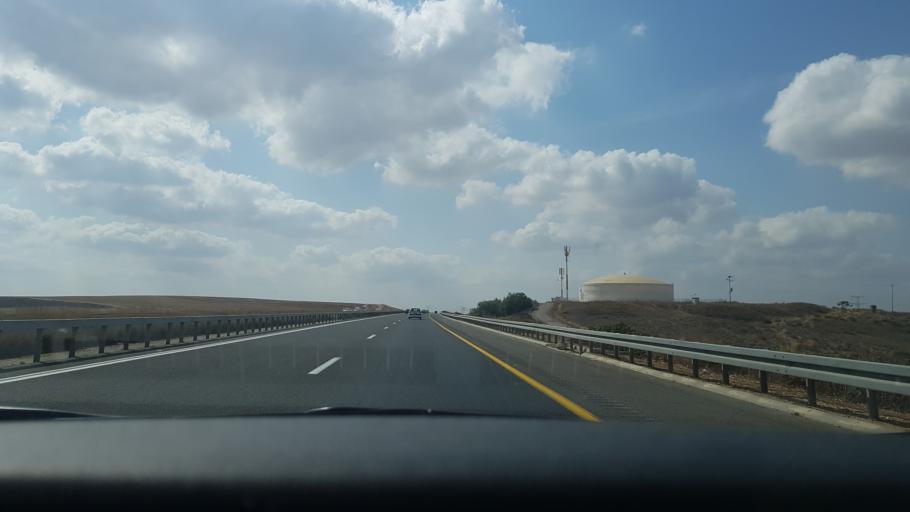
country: IL
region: Southern District
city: Qiryat Gat
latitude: 31.5442
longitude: 34.7980
